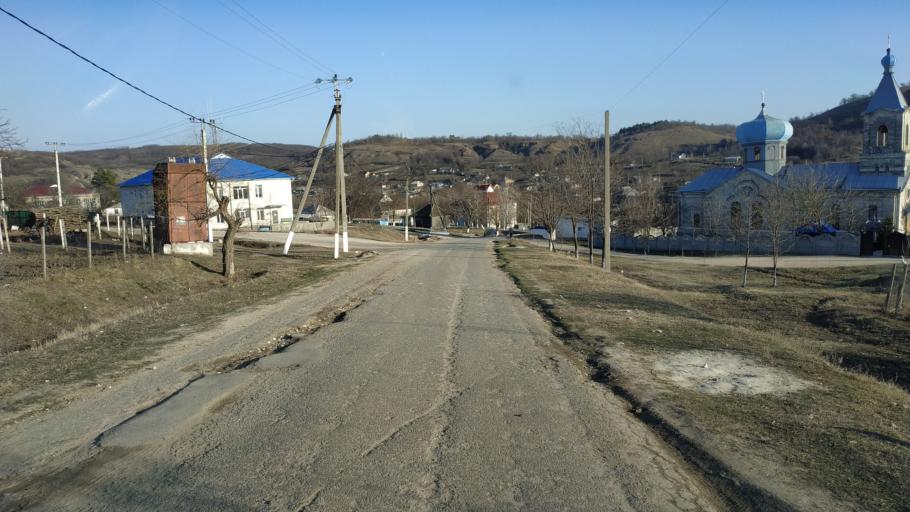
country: MD
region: Hincesti
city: Hincesti
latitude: 46.7003
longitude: 28.5430
